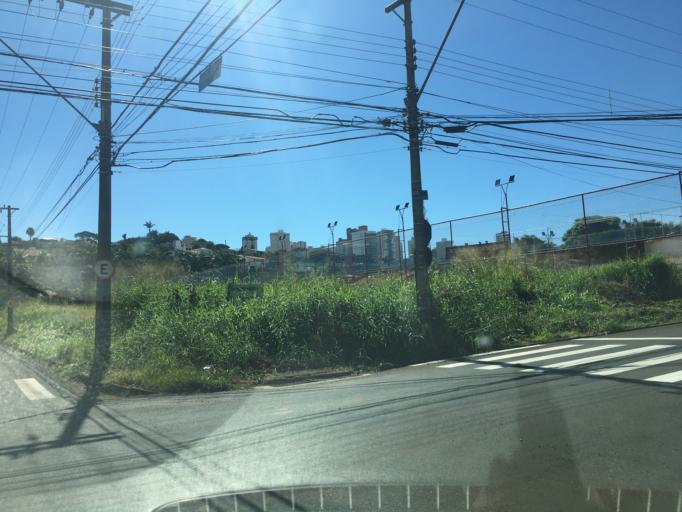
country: BR
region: Minas Gerais
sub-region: Uberlandia
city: Uberlandia
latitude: -18.9325
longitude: -48.2799
